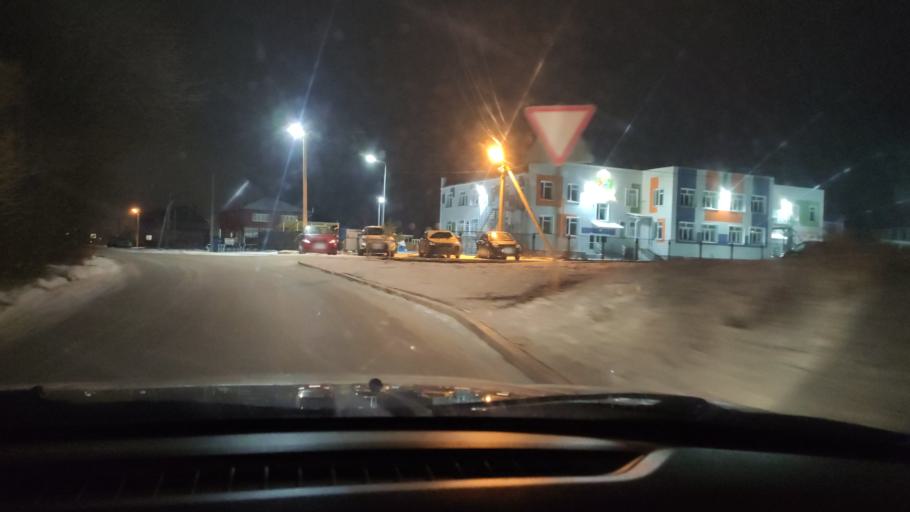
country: RU
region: Perm
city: Ferma
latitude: 57.8939
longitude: 56.3278
